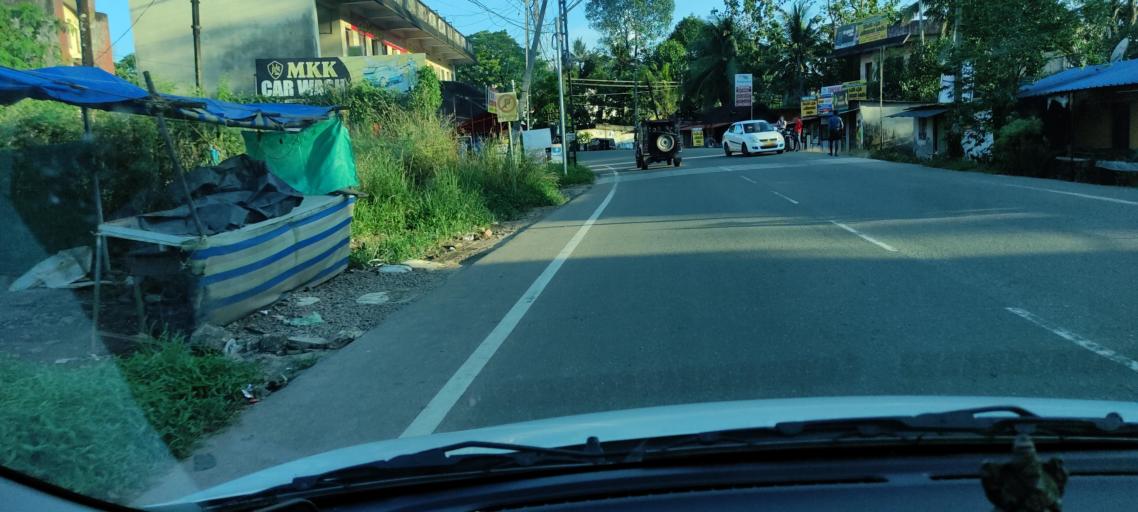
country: IN
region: Kerala
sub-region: Pattanamtitta
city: Adur
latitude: 9.1456
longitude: 76.7651
